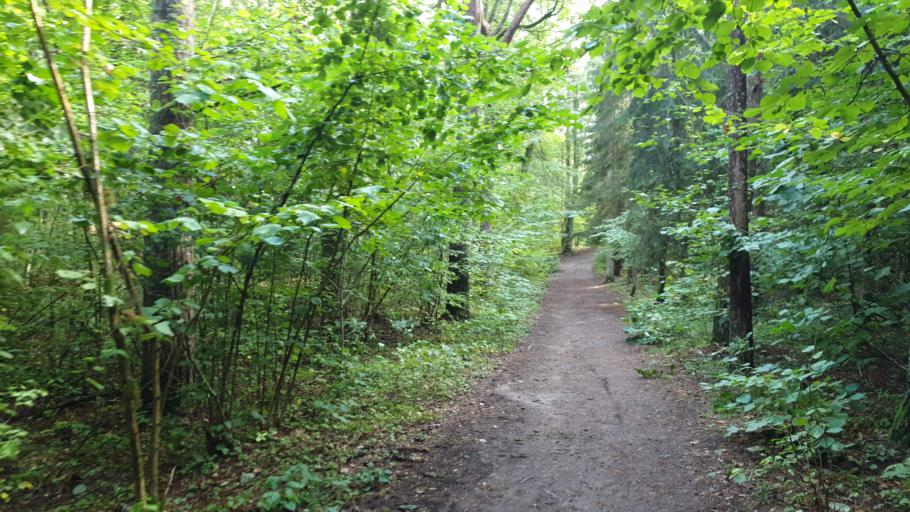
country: LT
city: Trakai
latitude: 54.6466
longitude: 24.9664
